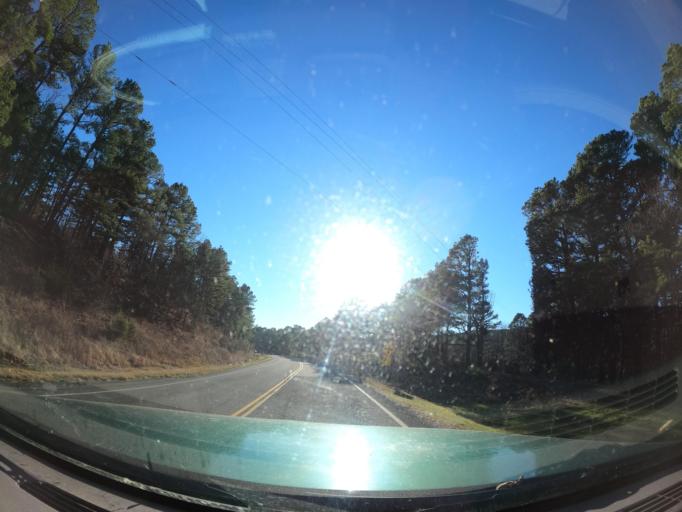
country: US
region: Oklahoma
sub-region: Latimer County
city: Wilburton
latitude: 34.9822
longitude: -95.3583
